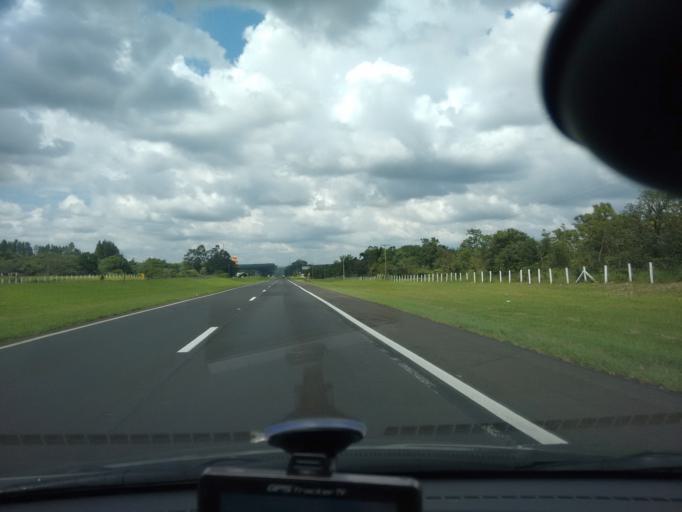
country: BR
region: Sao Paulo
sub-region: Sao Carlos
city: Sao Carlos
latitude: -22.0981
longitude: -47.8279
